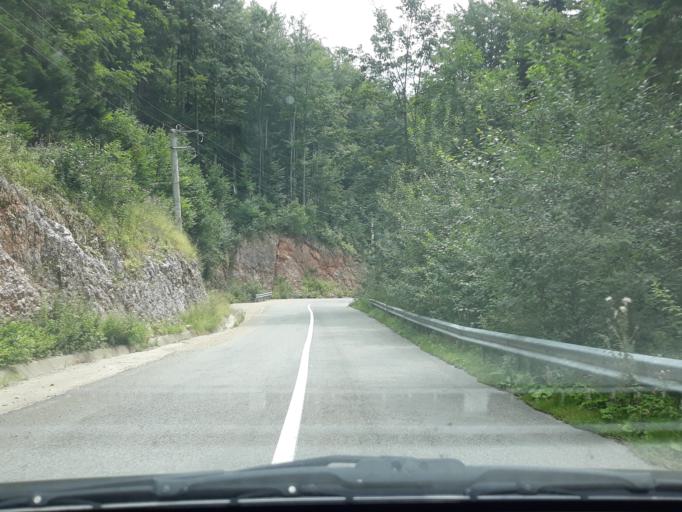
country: RO
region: Bihor
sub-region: Comuna Pietroasa
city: Pietroasa
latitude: 46.5918
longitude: 22.6754
